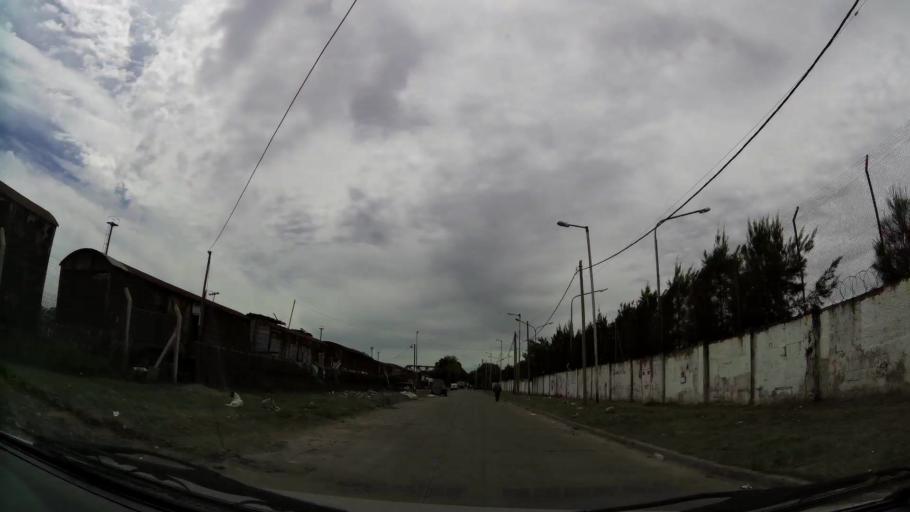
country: AR
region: Buenos Aires
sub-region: Partido de Avellaneda
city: Avellaneda
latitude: -34.6767
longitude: -58.3755
